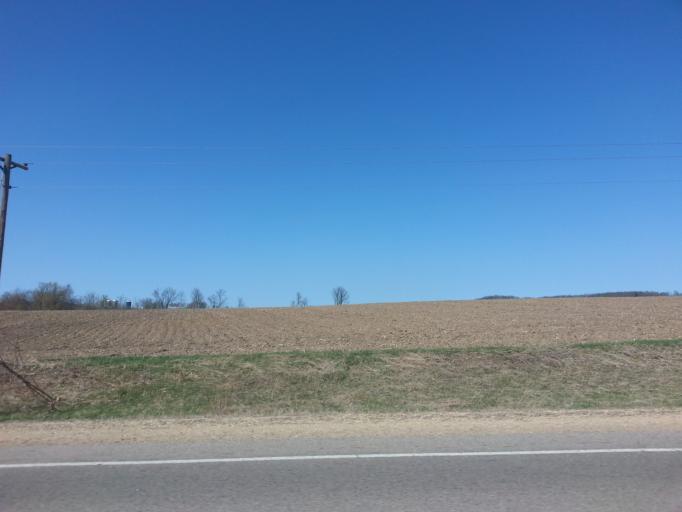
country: US
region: Wisconsin
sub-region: Dunn County
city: Menomonie
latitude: 44.8949
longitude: -91.9932
